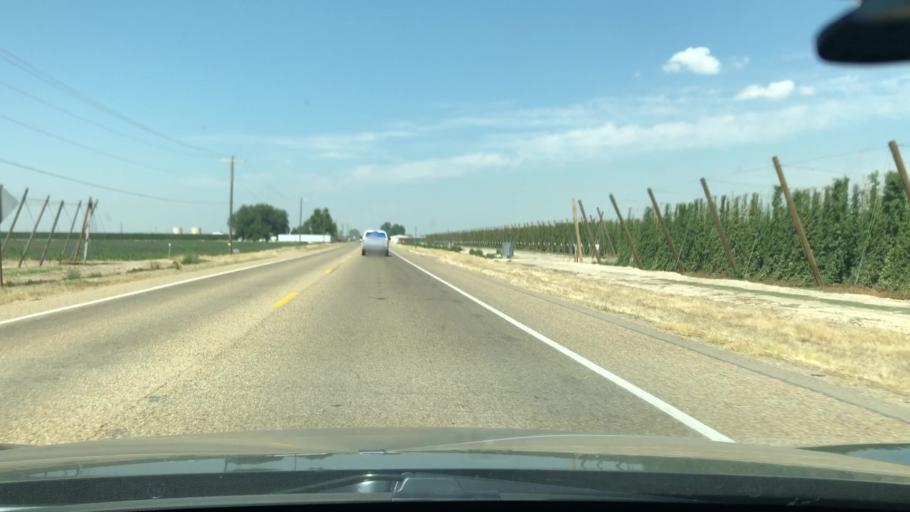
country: US
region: Idaho
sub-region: Canyon County
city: Wilder
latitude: 43.6862
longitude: -116.9120
